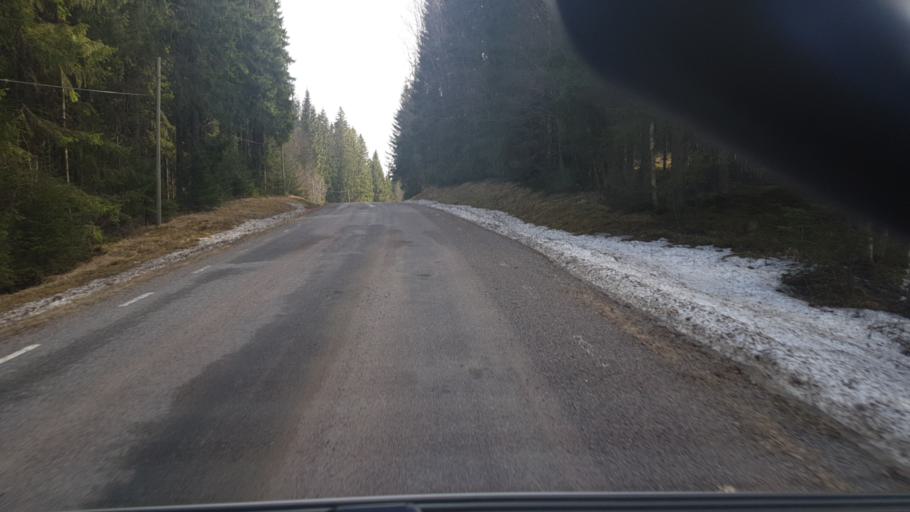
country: SE
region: Vaermland
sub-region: Eda Kommun
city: Amotfors
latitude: 59.8497
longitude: 12.4244
